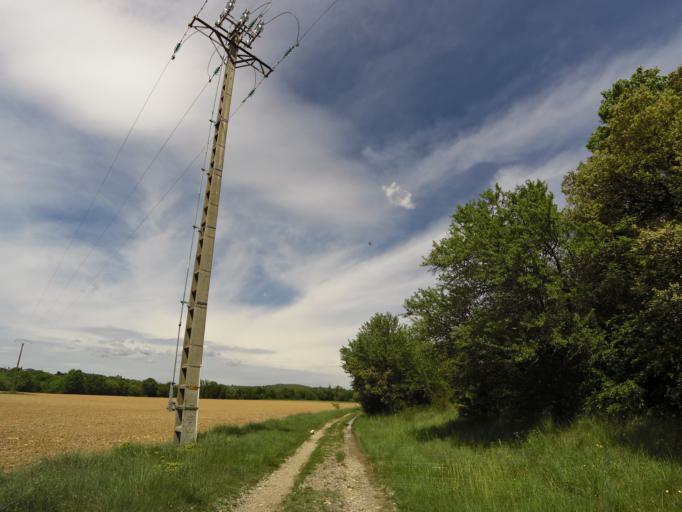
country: FR
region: Languedoc-Roussillon
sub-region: Departement du Gard
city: Quissac
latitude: 43.8777
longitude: 4.0286
